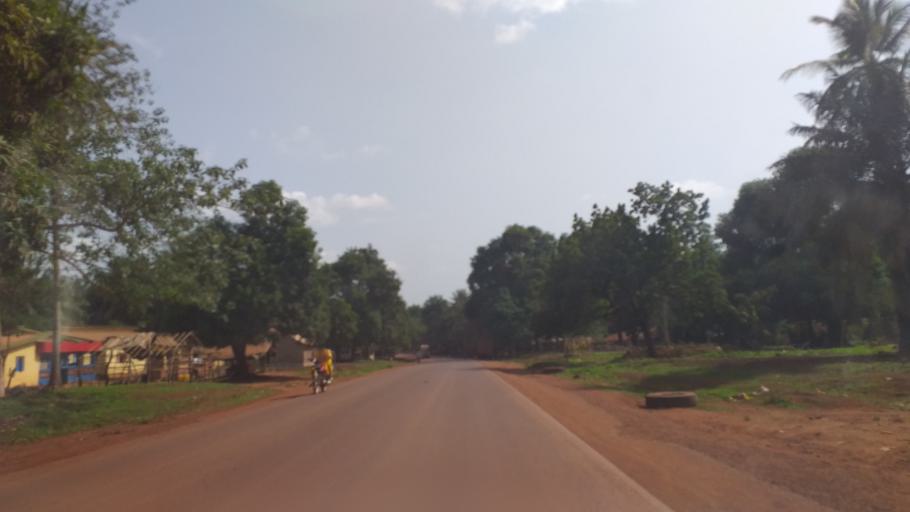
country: GN
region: Boke
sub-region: Boke Prefecture
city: Sangueya
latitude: 10.8142
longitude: -14.3820
